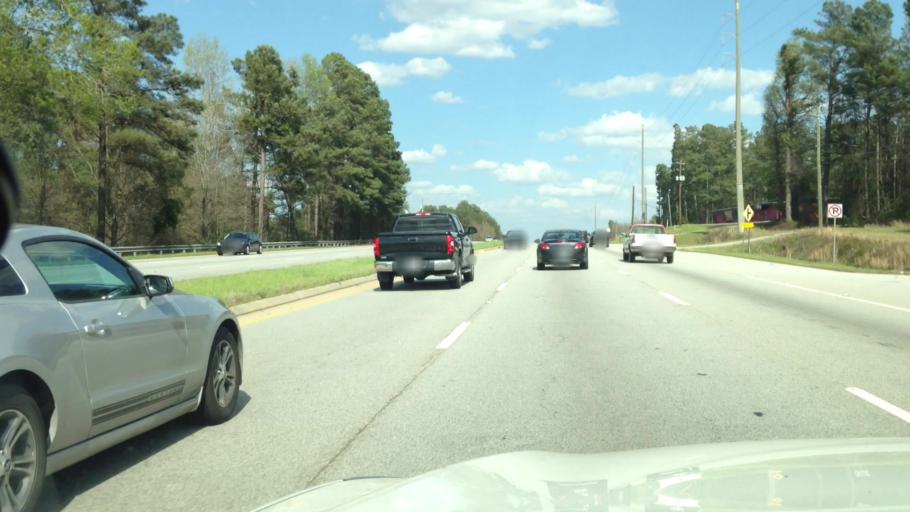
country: US
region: Georgia
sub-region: Columbia County
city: Martinez
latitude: 33.4445
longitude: -82.0948
